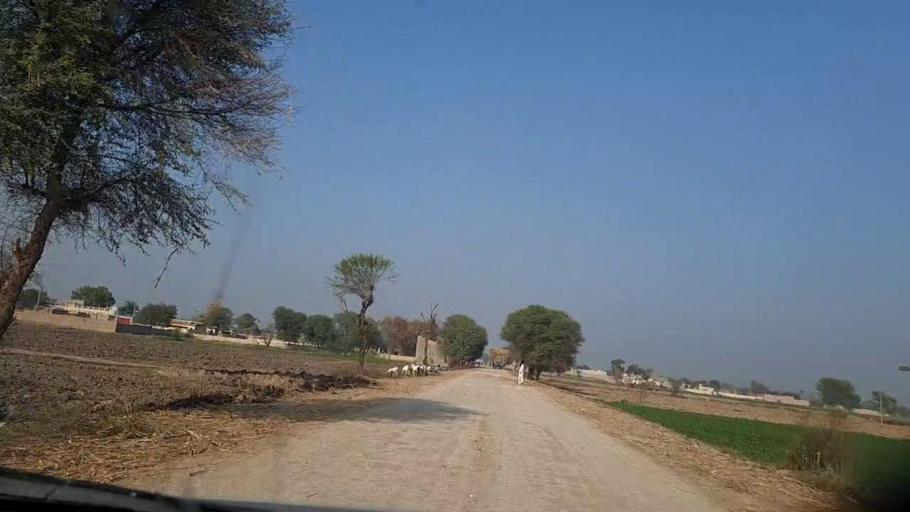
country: PK
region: Sindh
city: Moro
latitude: 26.7843
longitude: 67.9375
